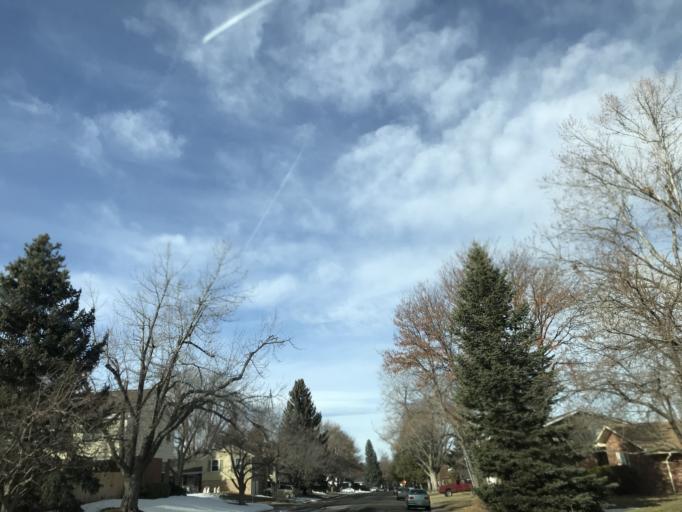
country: US
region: Colorado
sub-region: Arapahoe County
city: Littleton
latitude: 39.5936
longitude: -105.0115
